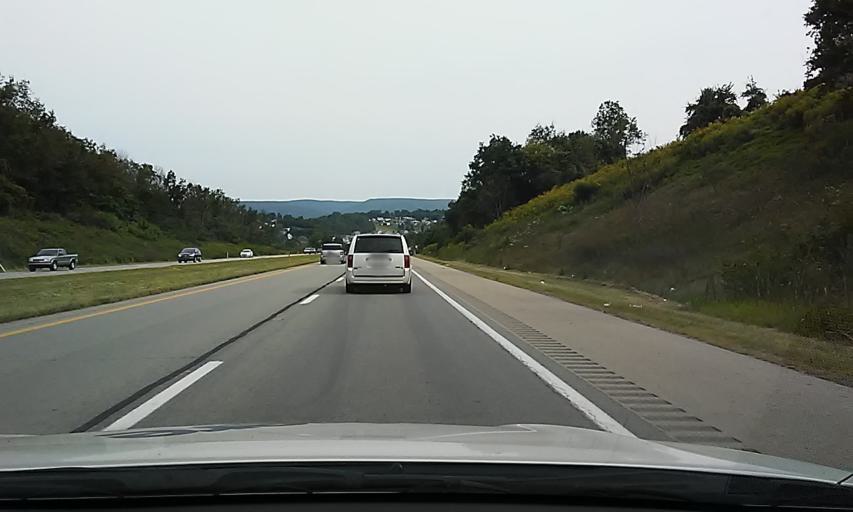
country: US
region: Pennsylvania
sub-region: Fayette County
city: South Uniontown
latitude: 39.8878
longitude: -79.7512
